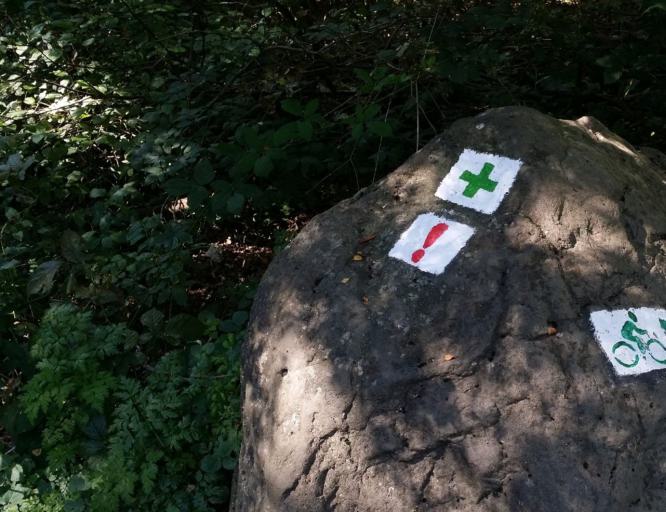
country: HU
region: Pest
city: Nagykovacsi
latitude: 47.6978
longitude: 18.9886
